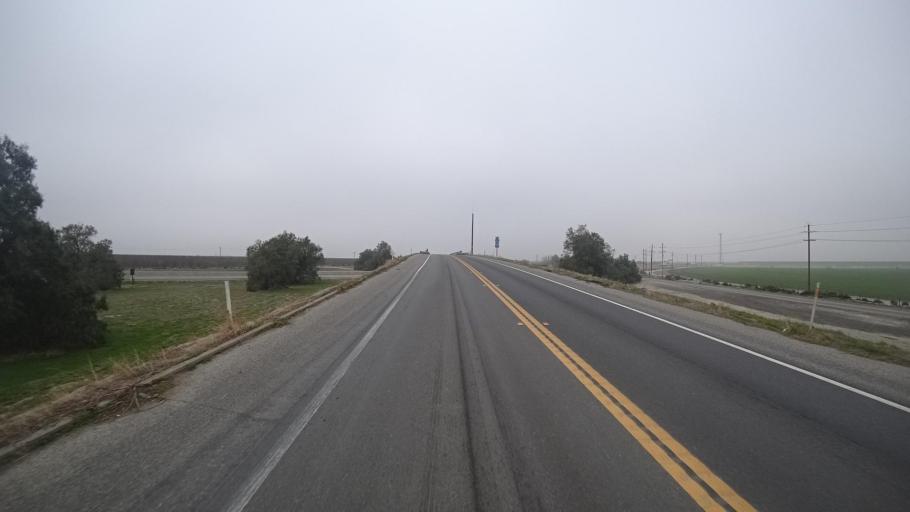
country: US
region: California
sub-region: Kern County
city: Greenfield
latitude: 35.2091
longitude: -119.1613
